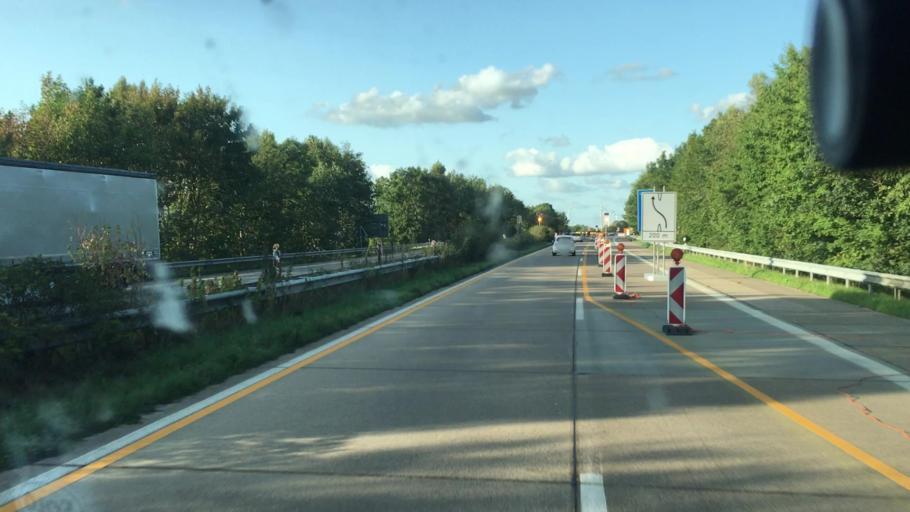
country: DE
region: Lower Saxony
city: Sande
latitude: 53.5146
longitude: 7.9978
